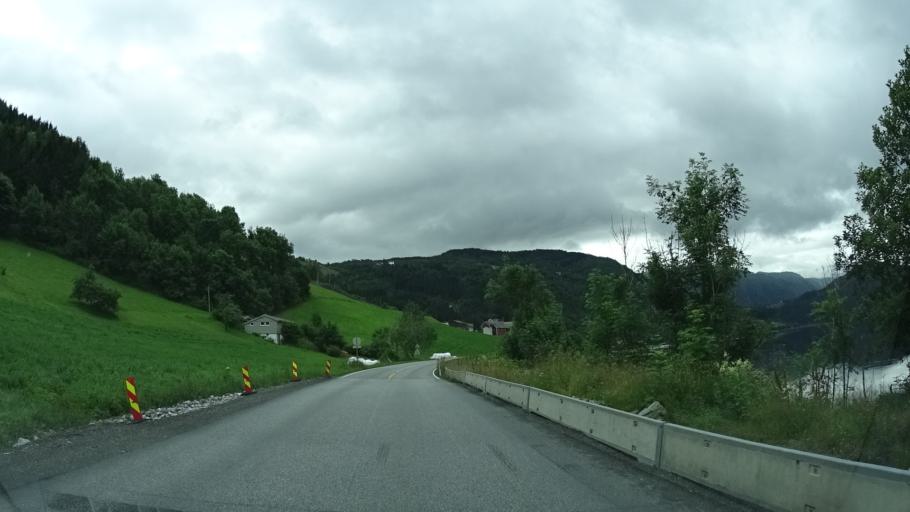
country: NO
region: Hordaland
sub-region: Granvin
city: Granvin
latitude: 60.5635
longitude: 6.7257
